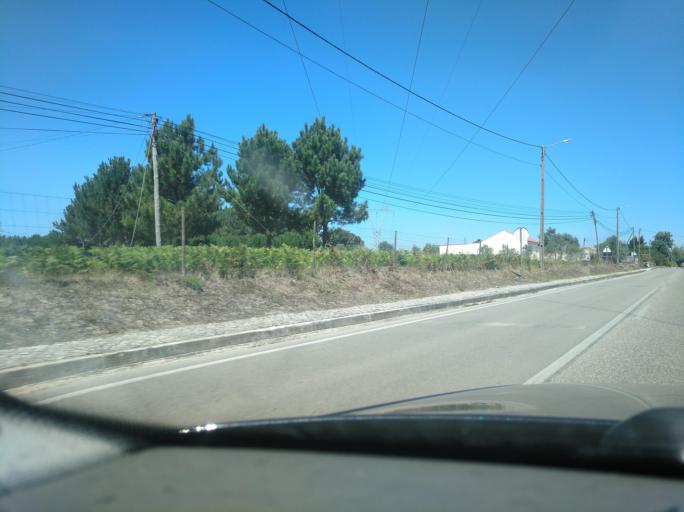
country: PT
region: Leiria
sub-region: Alcobaca
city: Aljubarrota
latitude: 39.5732
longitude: -8.9169
